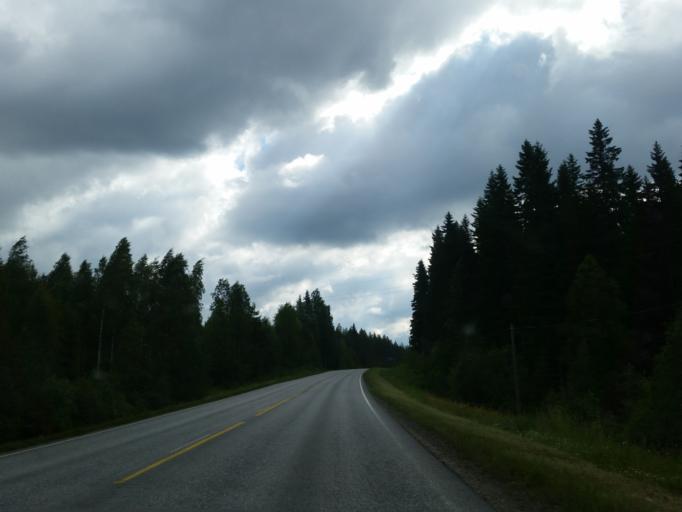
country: FI
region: Northern Savo
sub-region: Sisae-Savo
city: Suonenjoki
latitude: 62.8580
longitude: 27.2332
